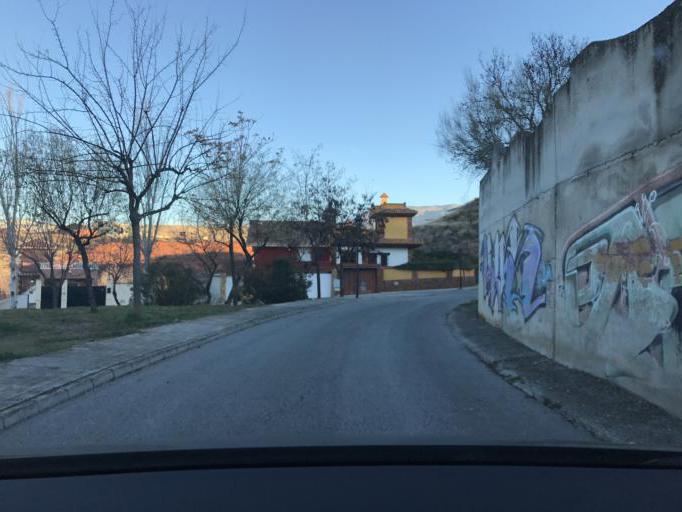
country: ES
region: Andalusia
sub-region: Provincia de Granada
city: Jun
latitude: 37.2186
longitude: -3.5899
